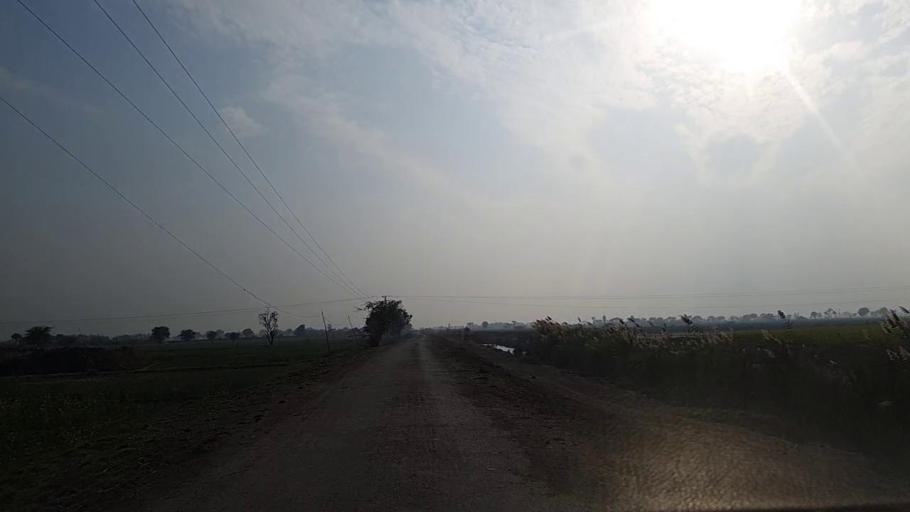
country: PK
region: Sindh
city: Jam Sahib
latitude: 26.3140
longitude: 68.5251
